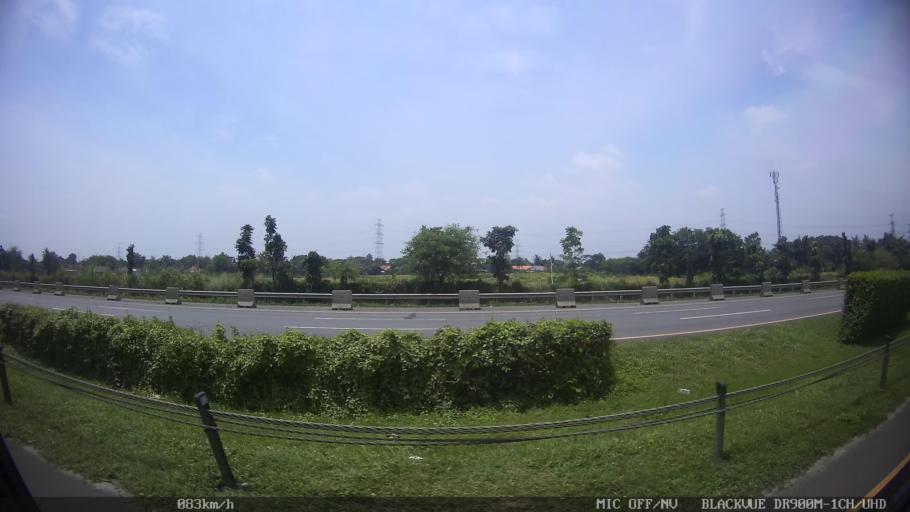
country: ID
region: West Java
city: Kresek
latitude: -6.1902
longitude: 106.4120
